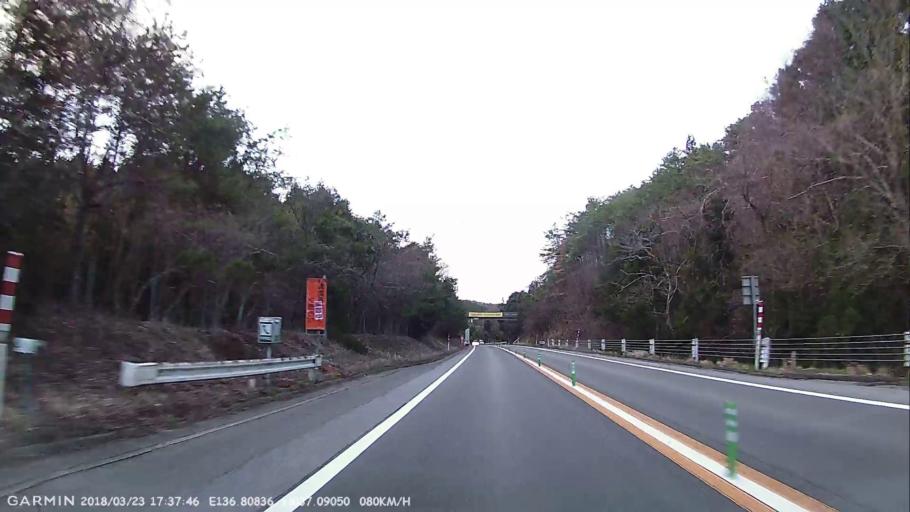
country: JP
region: Ishikawa
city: Nanao
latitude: 37.0908
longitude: 136.8084
